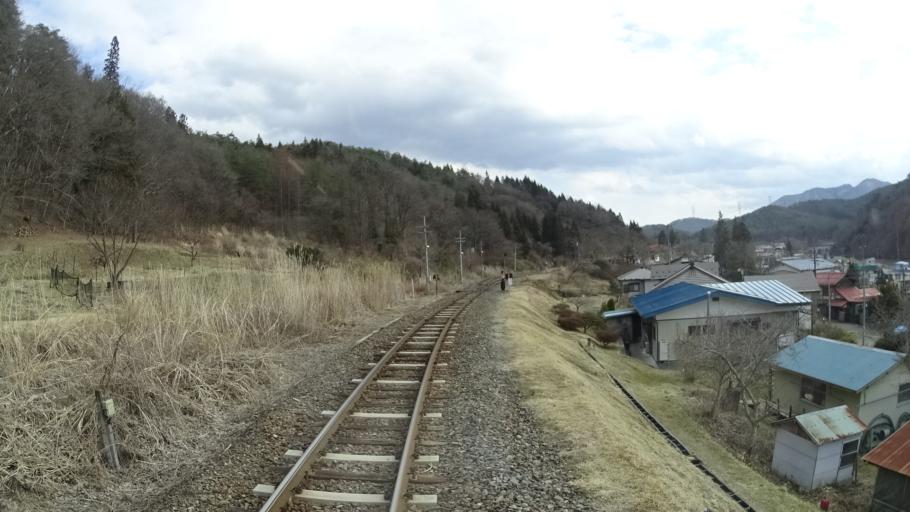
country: JP
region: Iwate
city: Tono
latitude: 39.3527
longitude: 141.3495
